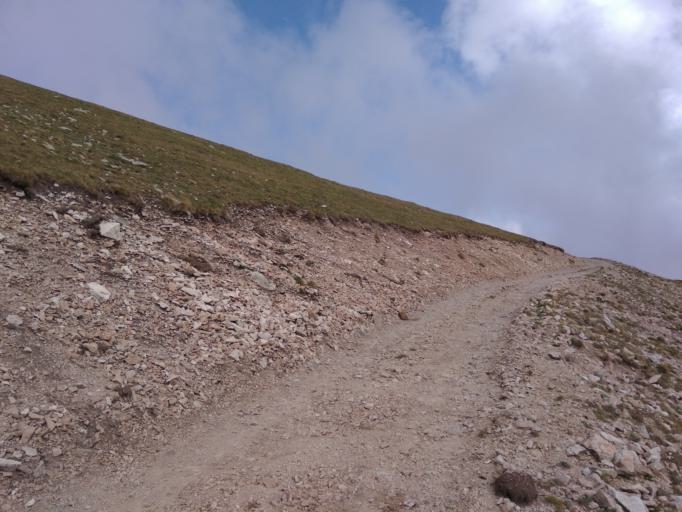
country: BG
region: Lovech
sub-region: Obshtina Apriltsi
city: Apriltsi
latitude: 42.7293
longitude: 24.9278
